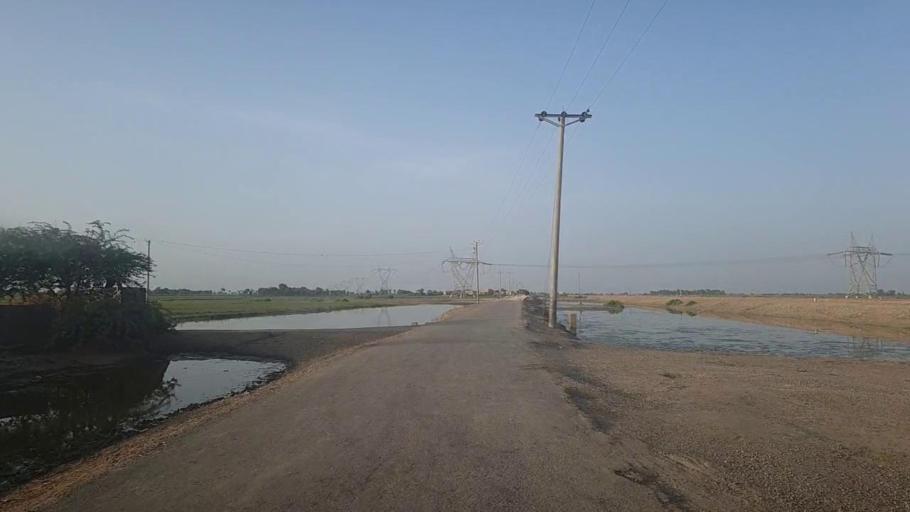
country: PK
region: Sindh
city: Radhan
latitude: 27.1196
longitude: 67.9171
